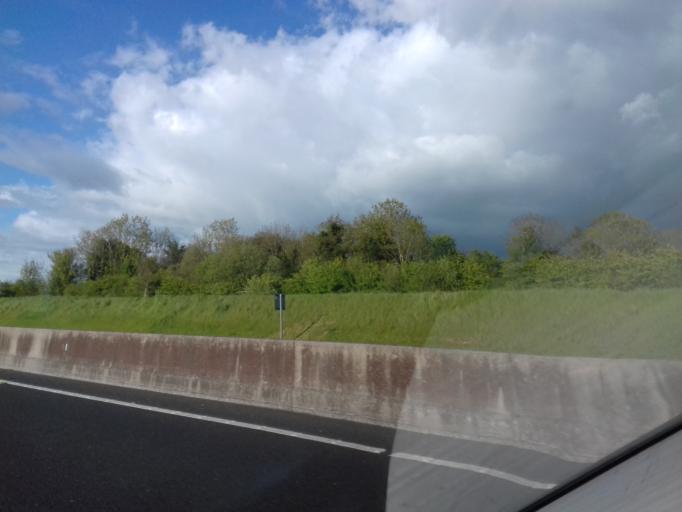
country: IE
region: Leinster
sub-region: Kildare
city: Castledermot
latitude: 52.9217
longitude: -6.8672
